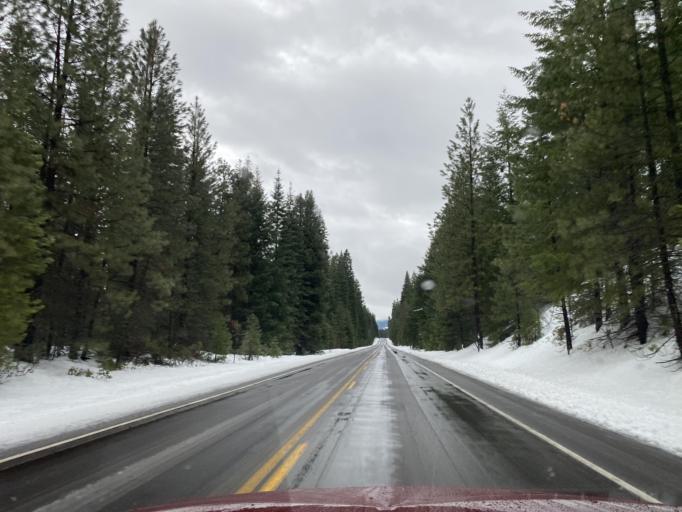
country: US
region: Oregon
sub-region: Klamath County
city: Klamath Falls
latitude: 42.5198
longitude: -122.0840
